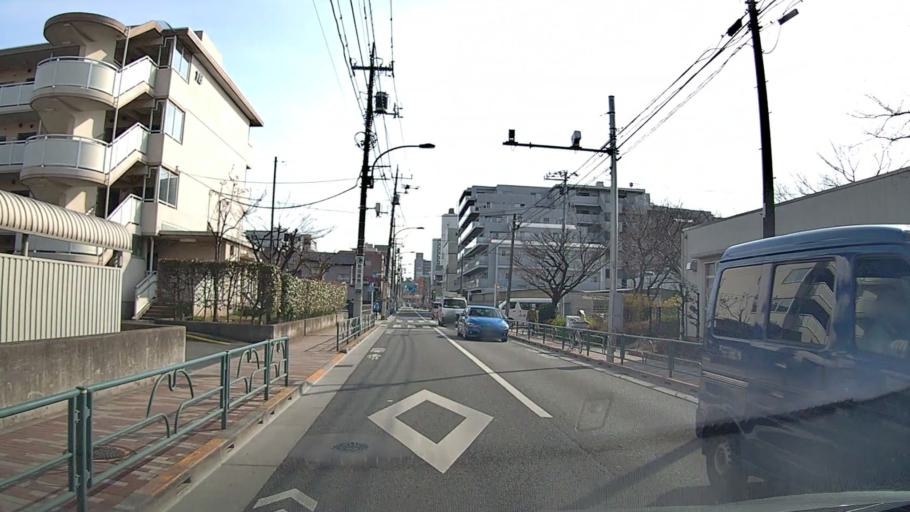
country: JP
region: Tokyo
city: Tokyo
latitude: 35.7307
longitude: 139.6544
